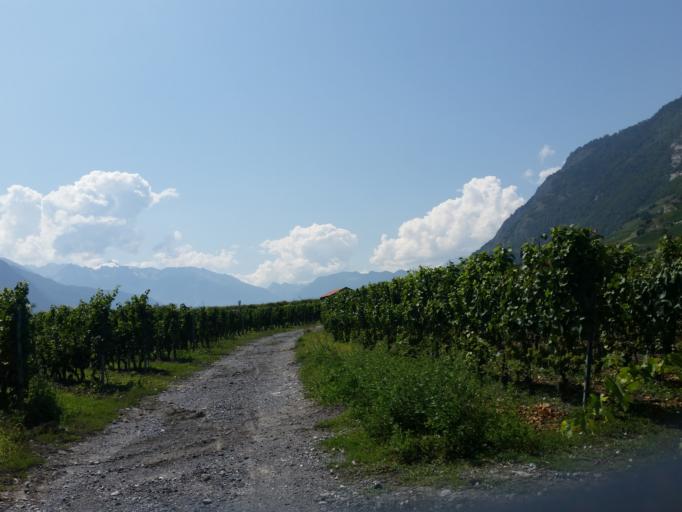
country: CH
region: Valais
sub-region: Martigny District
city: Leytron
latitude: 46.1777
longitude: 7.1993
